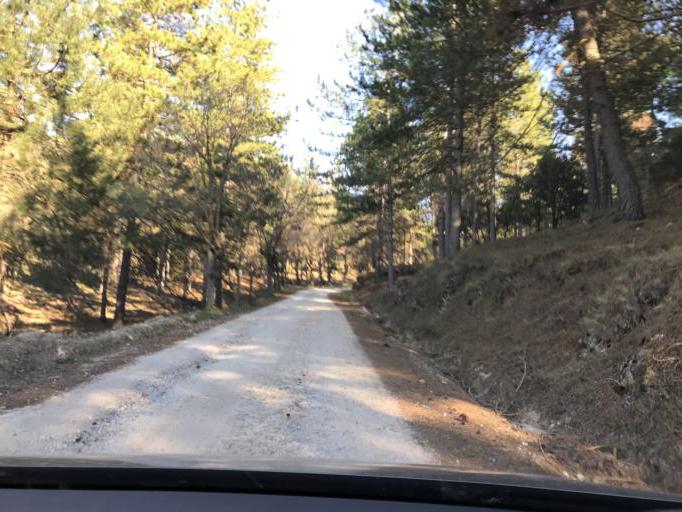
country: ES
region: Andalusia
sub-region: Provincia de Granada
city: Beas de Granada
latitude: 37.2536
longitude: -3.4680
